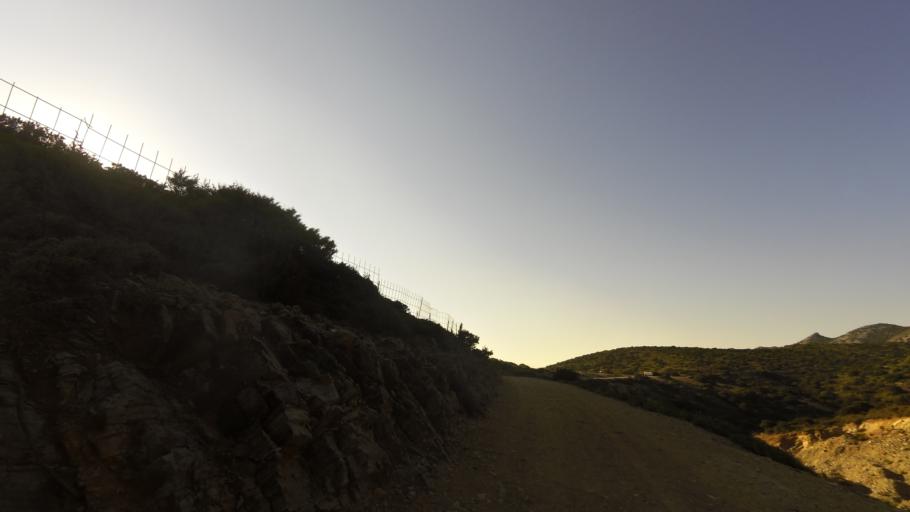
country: GR
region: South Aegean
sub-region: Nomos Kykladon
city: Antiparos
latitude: 36.9878
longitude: 25.0290
